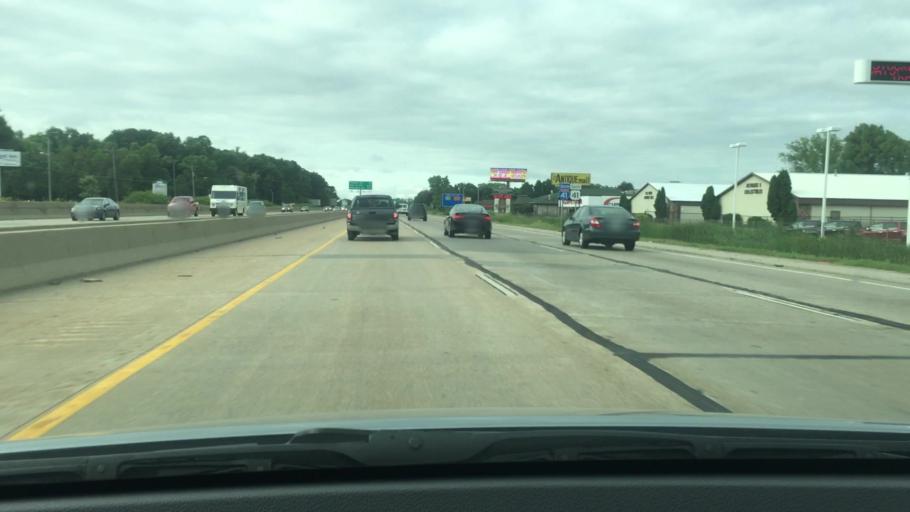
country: US
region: Wisconsin
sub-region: Outagamie County
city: Appleton
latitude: 44.2539
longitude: -88.4665
